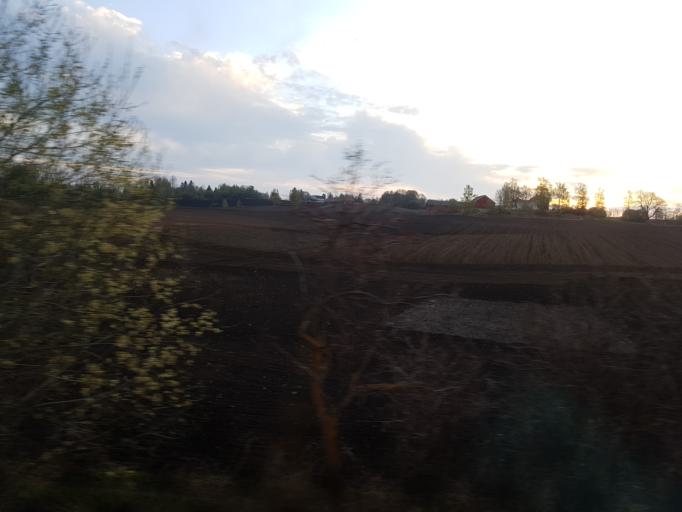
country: NO
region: Hedmark
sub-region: Stange
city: Stange
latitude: 60.7499
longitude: 11.1317
